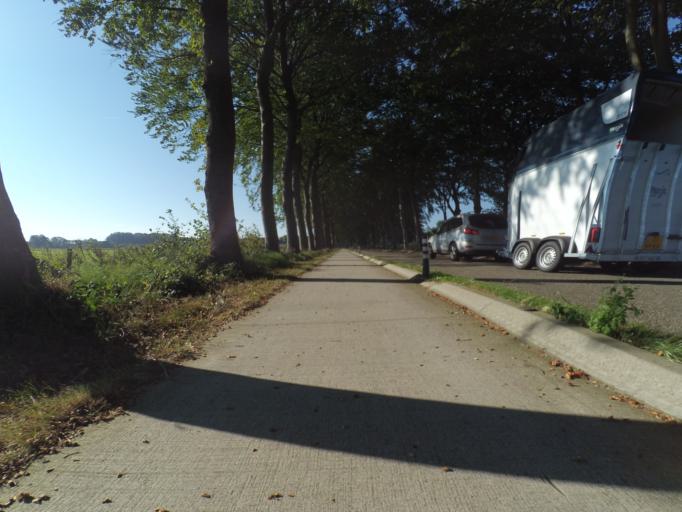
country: NL
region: Gelderland
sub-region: Gemeente Ermelo
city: Horst
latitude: 52.2771
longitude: 5.5703
